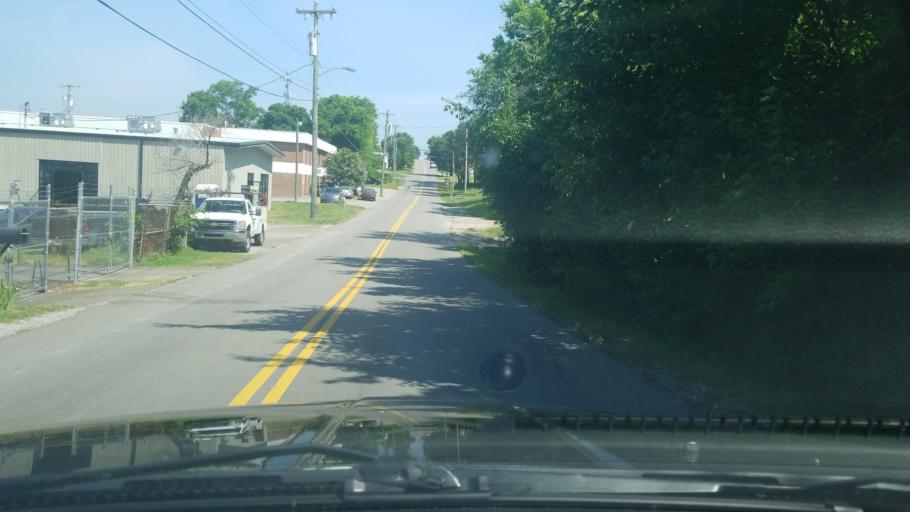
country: US
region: Tennessee
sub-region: Davidson County
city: Oak Hill
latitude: 36.1165
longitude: -86.7520
